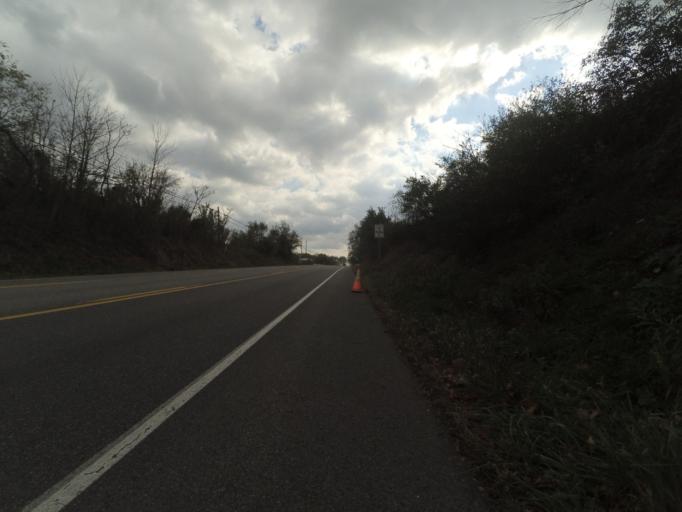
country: US
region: Pennsylvania
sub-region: Centre County
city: Bellefonte
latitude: 40.8986
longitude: -77.7894
